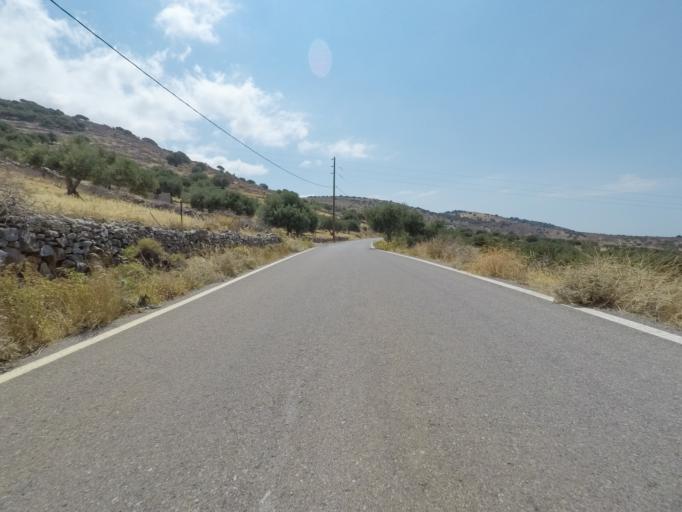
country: GR
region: Crete
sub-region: Nomos Lasithiou
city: Elounda
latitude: 35.3178
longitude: 25.6827
